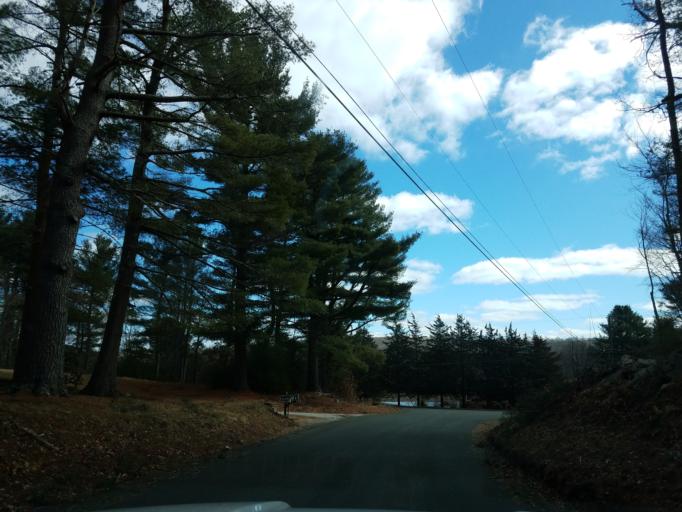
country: US
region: Massachusetts
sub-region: Worcester County
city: Dudley
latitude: 42.0213
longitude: -71.9149
